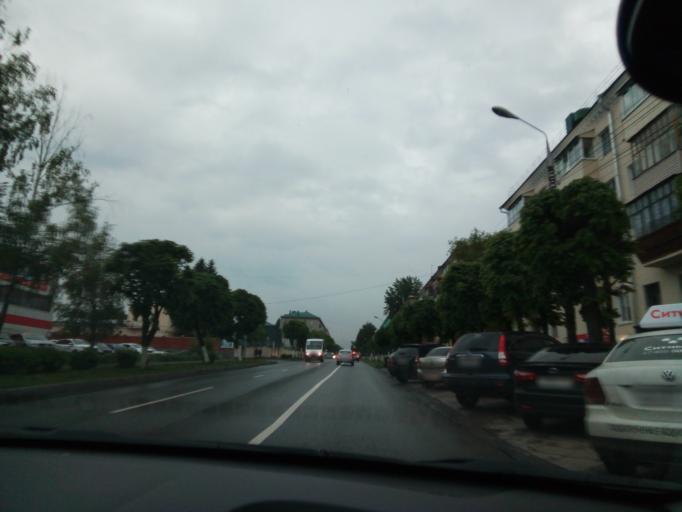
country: RU
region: Chuvashia
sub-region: Cheboksarskiy Rayon
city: Cheboksary
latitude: 56.1237
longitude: 47.2568
